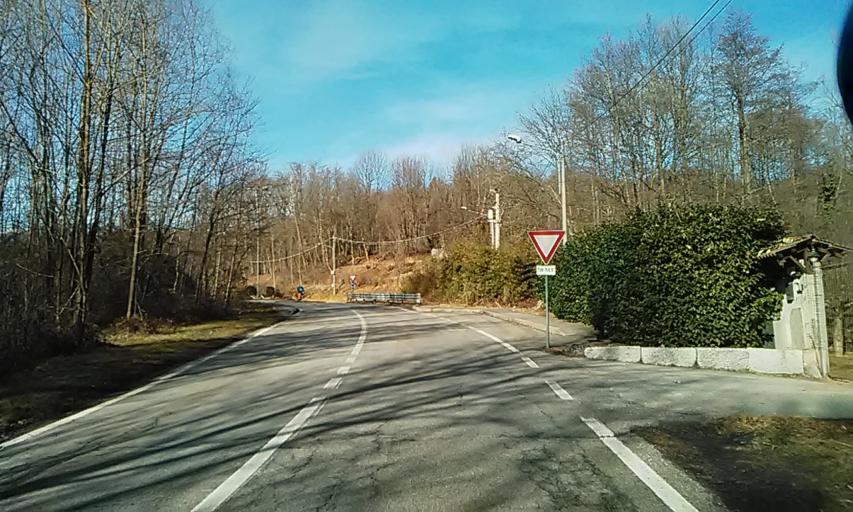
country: IT
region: Piedmont
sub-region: Provincia di Vercelli
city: Valduggia
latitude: 45.7242
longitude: 8.3039
